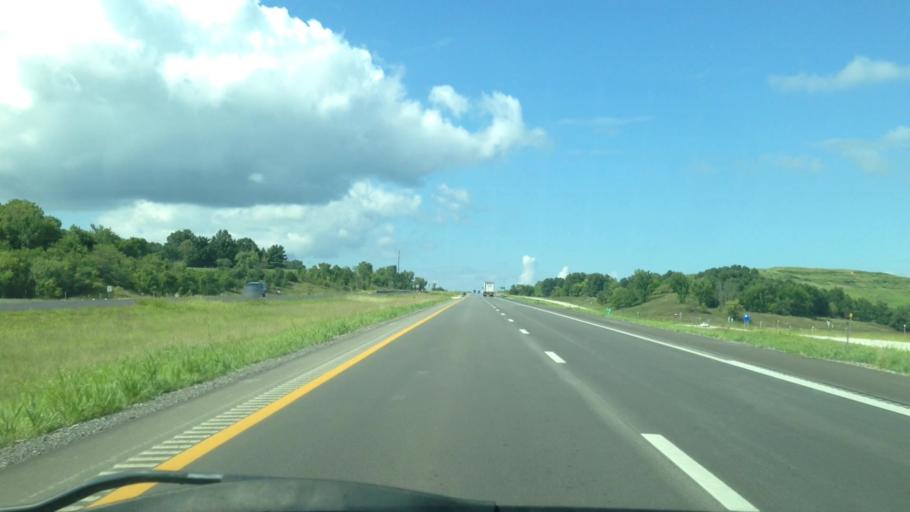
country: US
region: Illinois
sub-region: Adams County
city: Quincy
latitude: 40.0086
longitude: -91.5263
